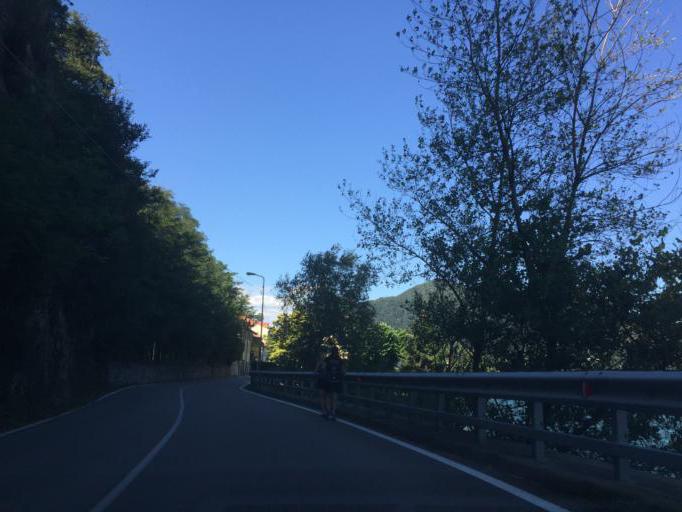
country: IT
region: Lombardy
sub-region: Provincia di Varese
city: Porto Ceresio
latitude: 45.9093
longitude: 8.8978
